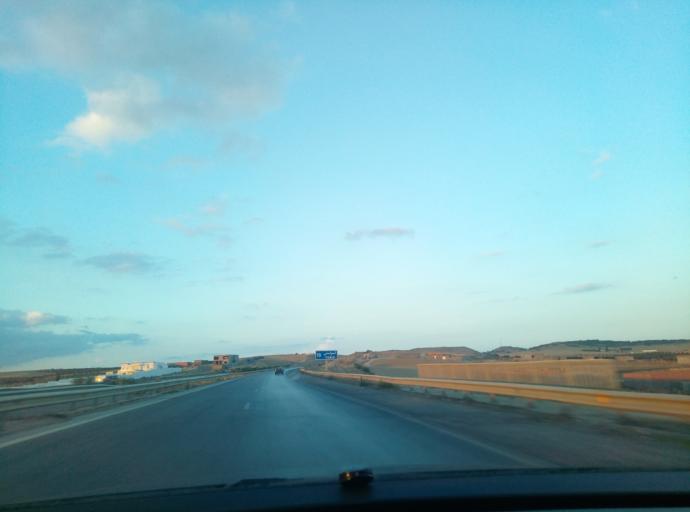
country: TN
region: Manouba
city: Manouba
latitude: 36.7483
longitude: 10.0381
